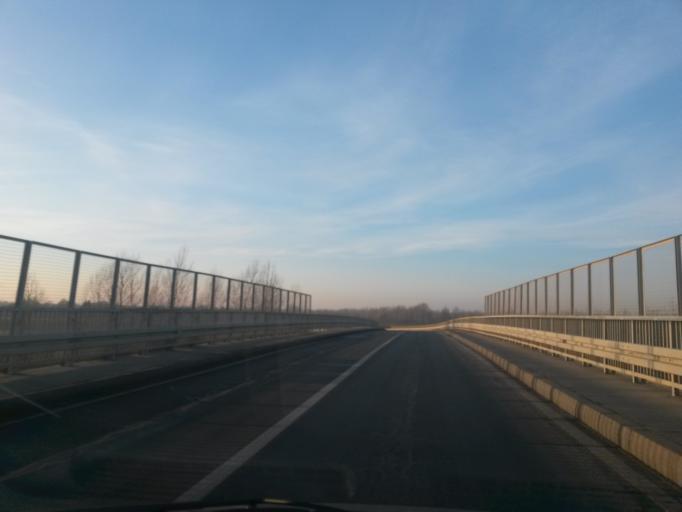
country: HR
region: Varazdinska
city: Jalzabet
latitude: 46.2946
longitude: 16.4944
